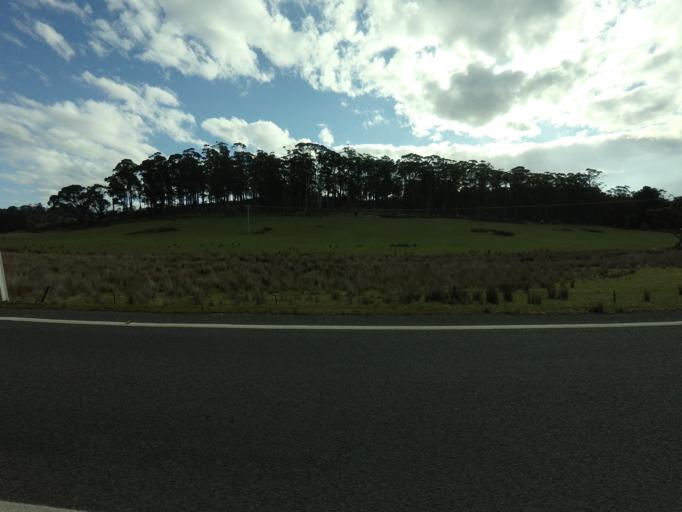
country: AU
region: Tasmania
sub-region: Sorell
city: Sorell
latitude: -42.6240
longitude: 147.6326
